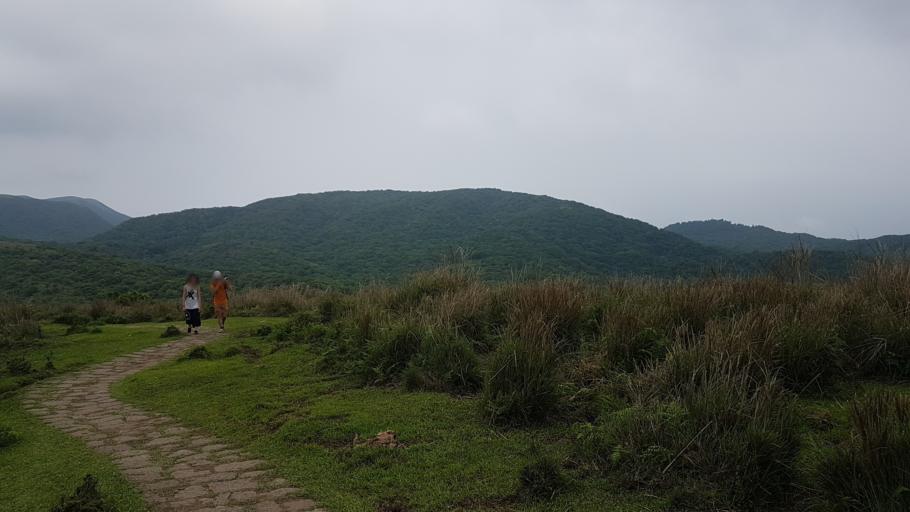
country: TW
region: Taipei
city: Taipei
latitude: 25.1607
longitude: 121.5757
